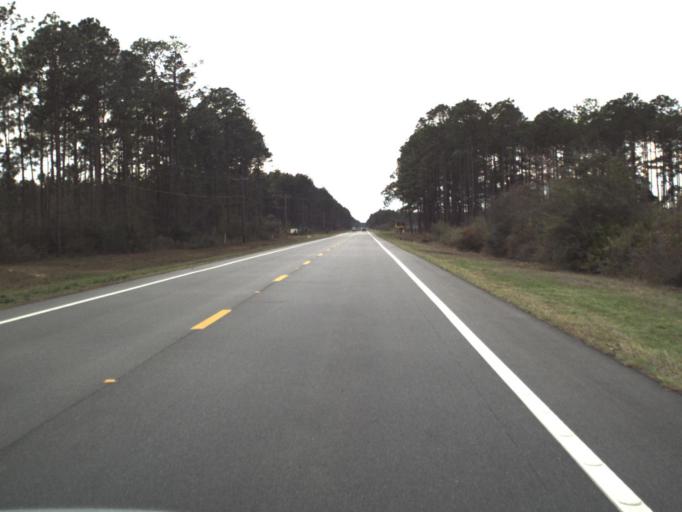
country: US
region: Florida
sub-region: Gulf County
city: Wewahitchka
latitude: 30.1409
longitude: -85.2687
